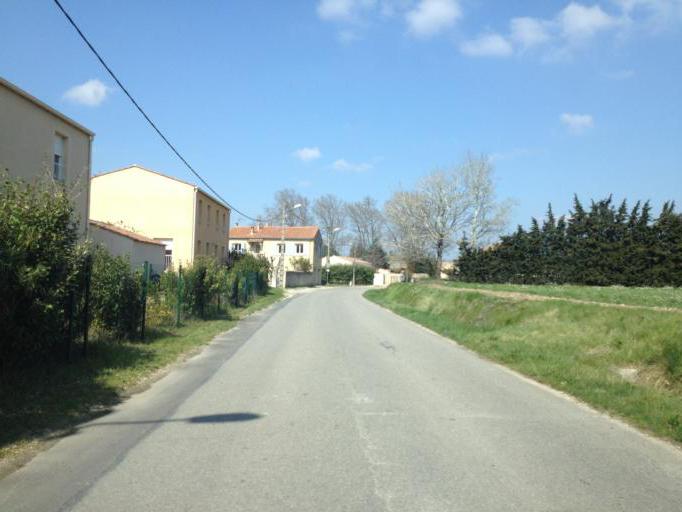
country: FR
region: Provence-Alpes-Cote d'Azur
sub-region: Departement du Vaucluse
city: Jonquieres
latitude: 44.1182
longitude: 4.9037
